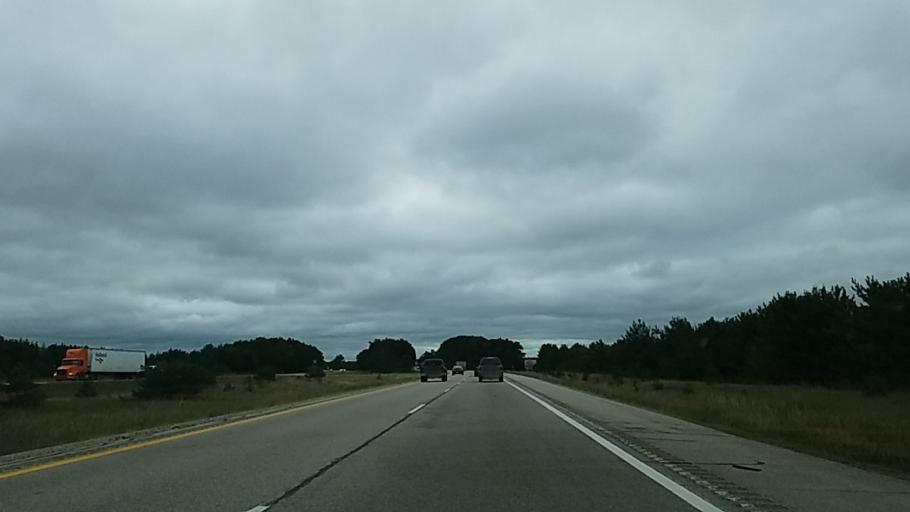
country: US
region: Michigan
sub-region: Otsego County
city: Gaylord
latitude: 45.0376
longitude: -84.6900
